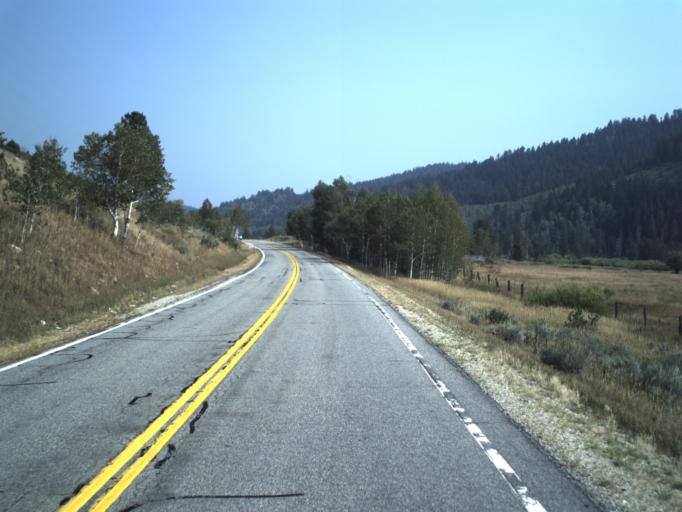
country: US
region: Utah
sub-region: Summit County
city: Francis
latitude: 40.6248
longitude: -111.1586
